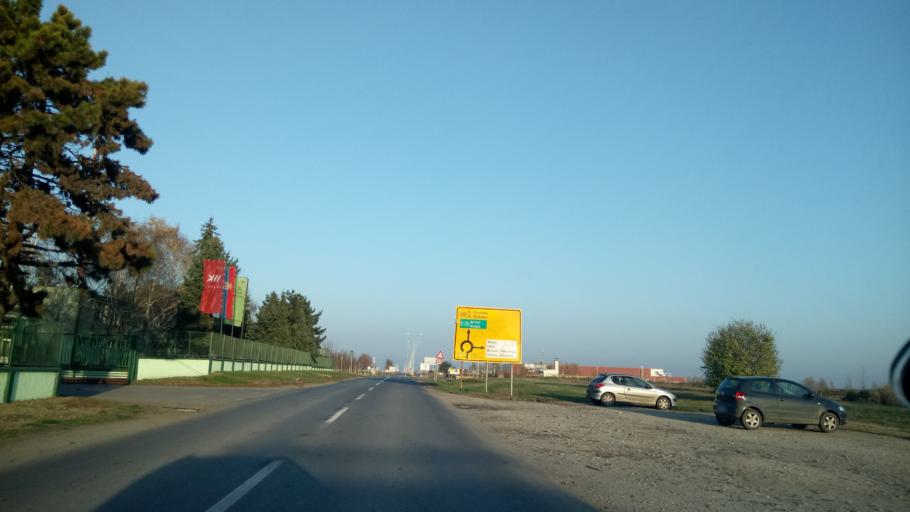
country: RS
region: Autonomna Pokrajina Vojvodina
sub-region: Sremski Okrug
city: Ingija
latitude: 45.0546
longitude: 20.1006
